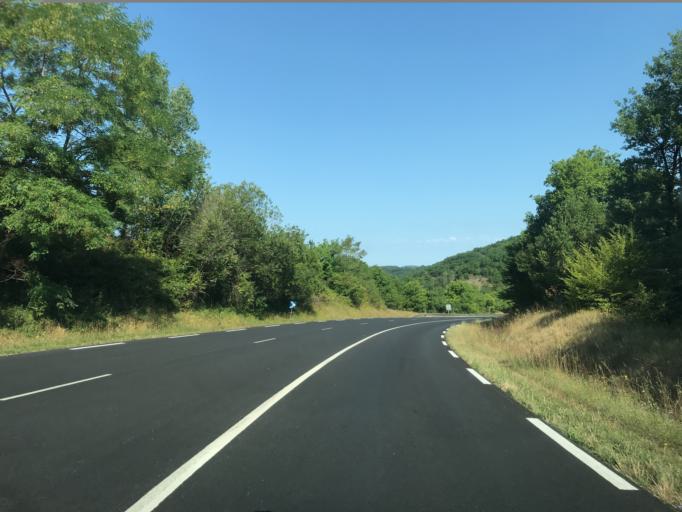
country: FR
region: Aquitaine
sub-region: Departement de la Dordogne
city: Montignac
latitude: 45.0492
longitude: 1.2144
